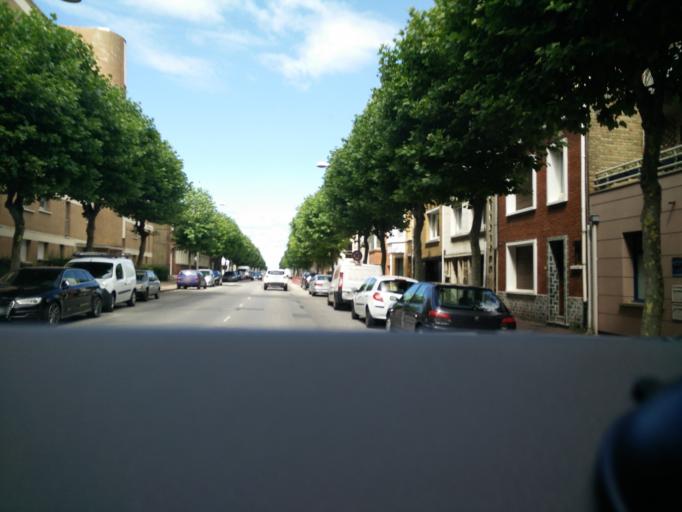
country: FR
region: Nord-Pas-de-Calais
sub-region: Departement du Nord
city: Coudekerque-Branche
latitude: 51.0456
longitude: 2.4033
